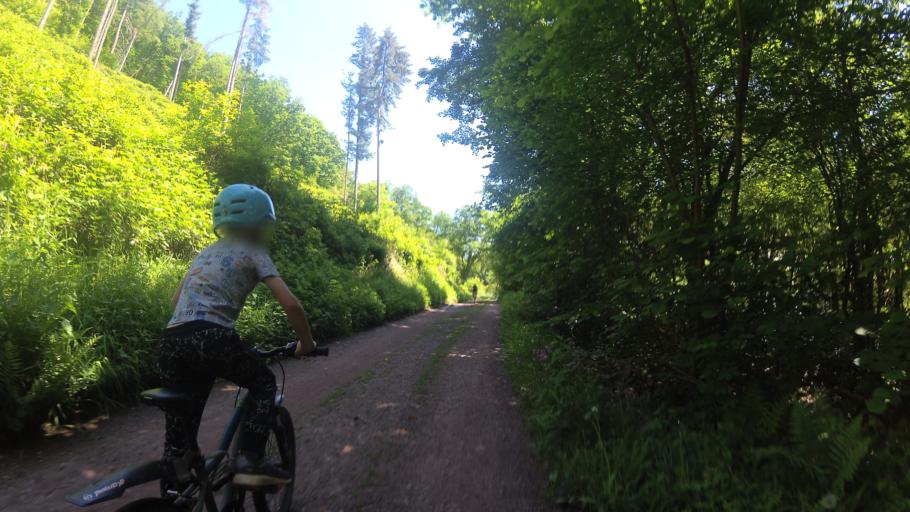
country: DE
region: Saarland
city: Mettlach
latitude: 49.4868
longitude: 6.5692
